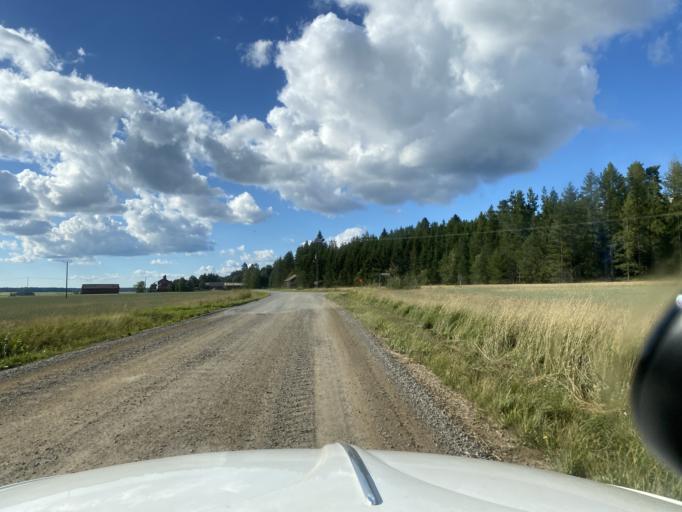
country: FI
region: Pirkanmaa
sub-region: Lounais-Pirkanmaa
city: Punkalaidun
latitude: 61.1434
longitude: 23.2016
